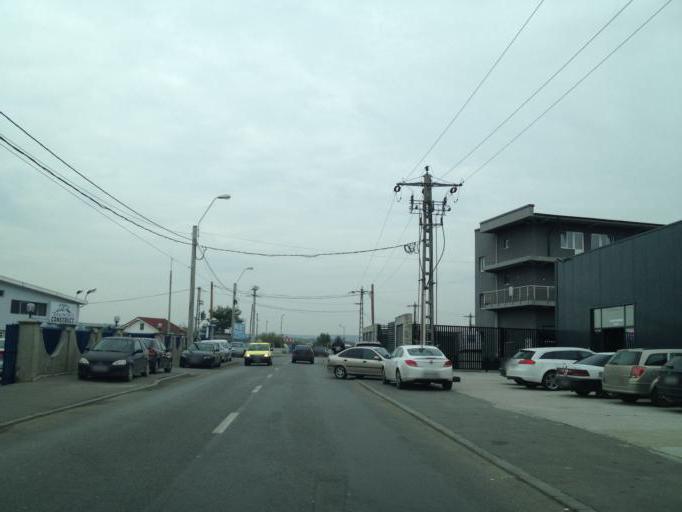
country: RO
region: Dolj
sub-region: Municipiul Craiova
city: Popoveni
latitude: 44.2869
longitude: 23.7965
